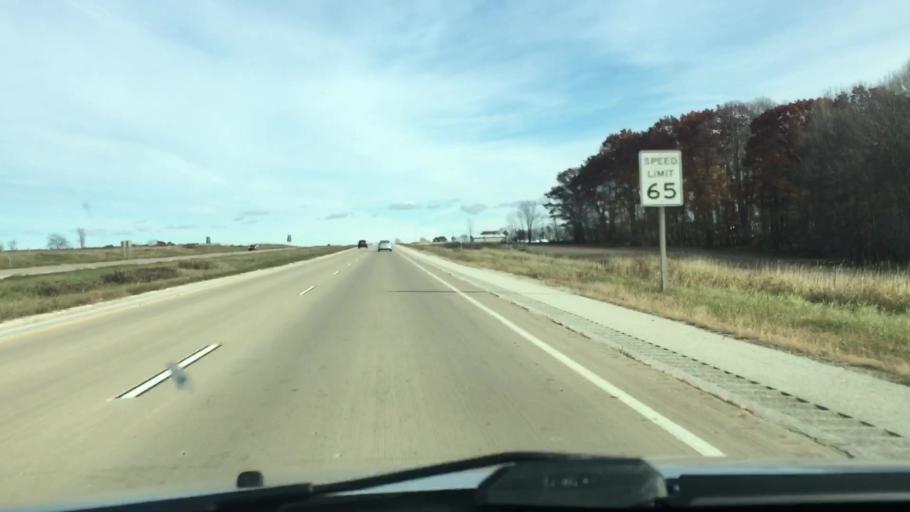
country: US
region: Wisconsin
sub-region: Kewaunee County
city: Luxemburg
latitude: 44.7168
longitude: -87.6693
